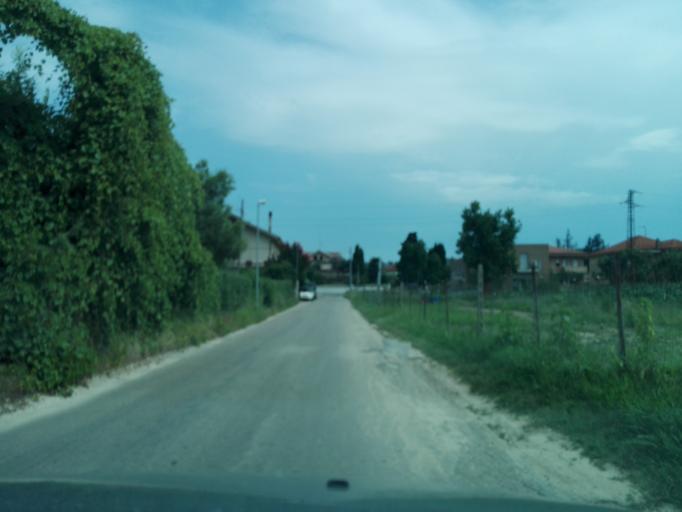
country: IT
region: Abruzzo
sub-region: Provincia di Pescara
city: Cappelle sul Tavo
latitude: 42.4839
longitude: 14.1154
